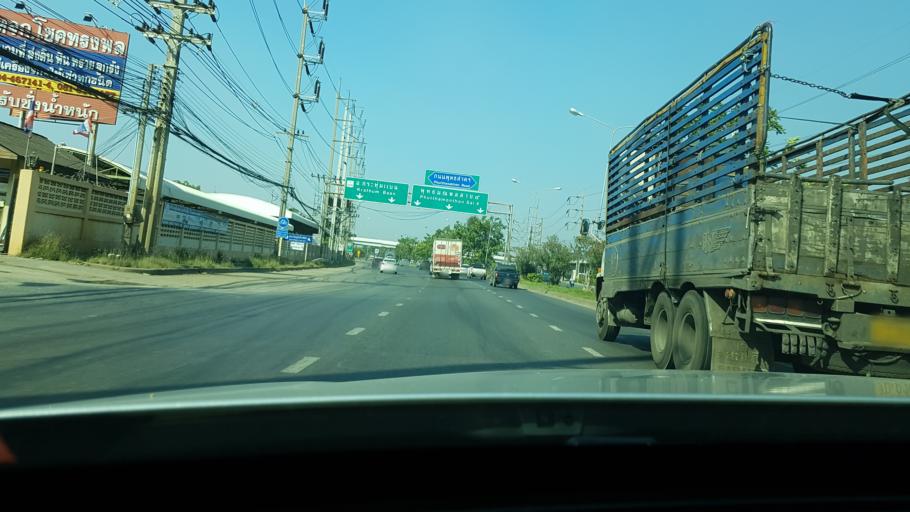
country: TH
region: Samut Sakhon
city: Krathum Baen
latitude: 13.6420
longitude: 100.2990
